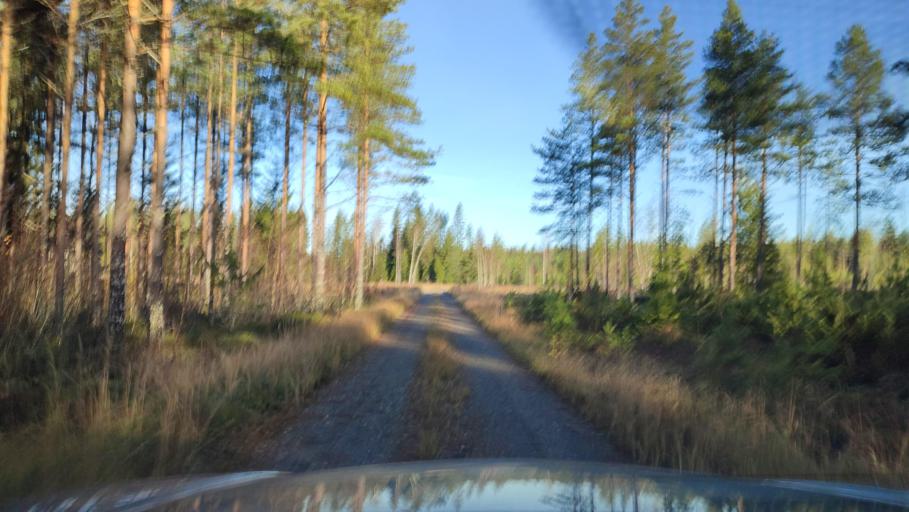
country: FI
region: Southern Ostrobothnia
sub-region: Suupohja
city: Karijoki
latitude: 62.1929
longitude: 21.6066
